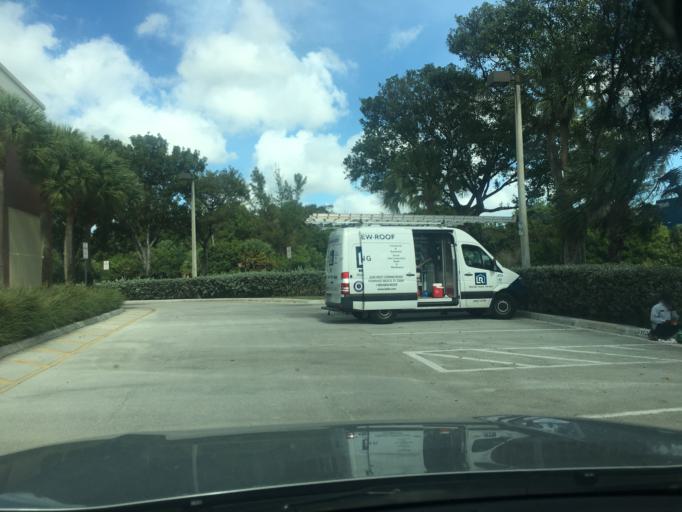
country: US
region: Florida
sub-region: Broward County
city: Broadview Park
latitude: 26.0744
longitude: -80.1784
